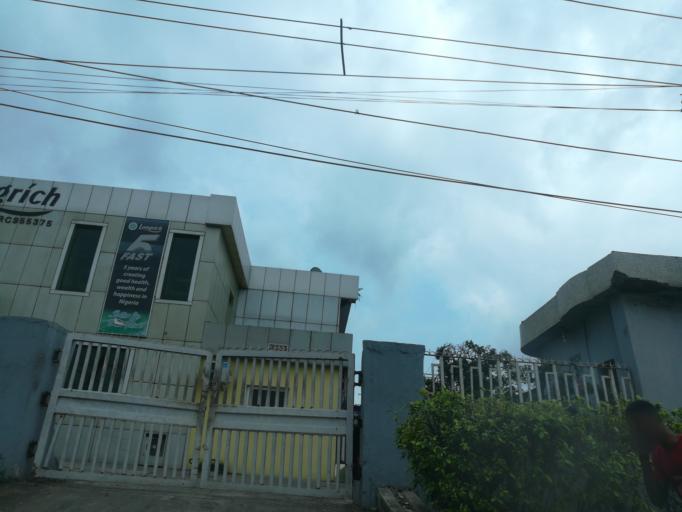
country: NG
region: Lagos
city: Ojota
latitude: 6.5866
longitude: 3.3637
